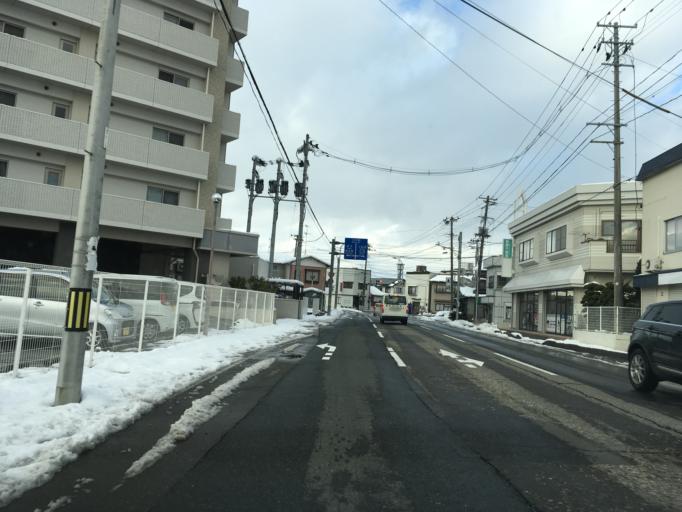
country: JP
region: Iwate
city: Mizusawa
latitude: 39.1360
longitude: 141.1450
